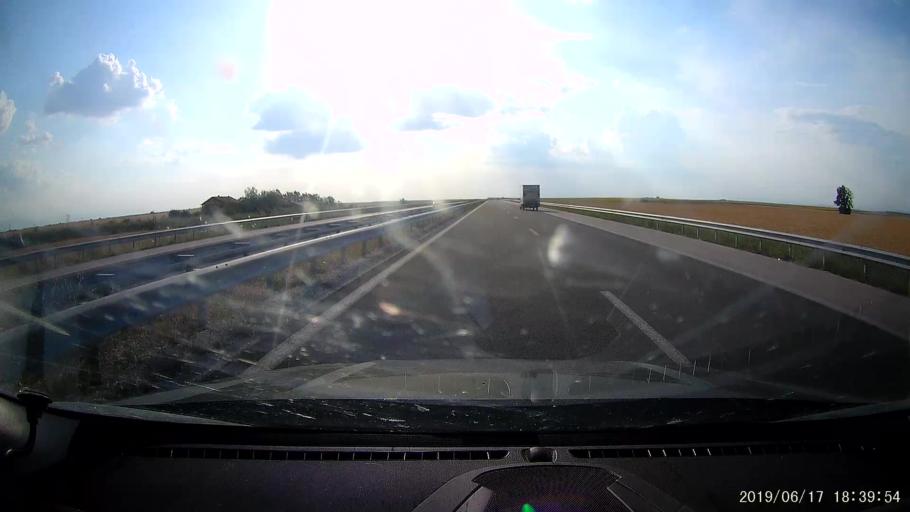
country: BG
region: Stara Zagora
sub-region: Obshtina Chirpan
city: Chirpan
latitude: 42.1496
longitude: 25.2934
